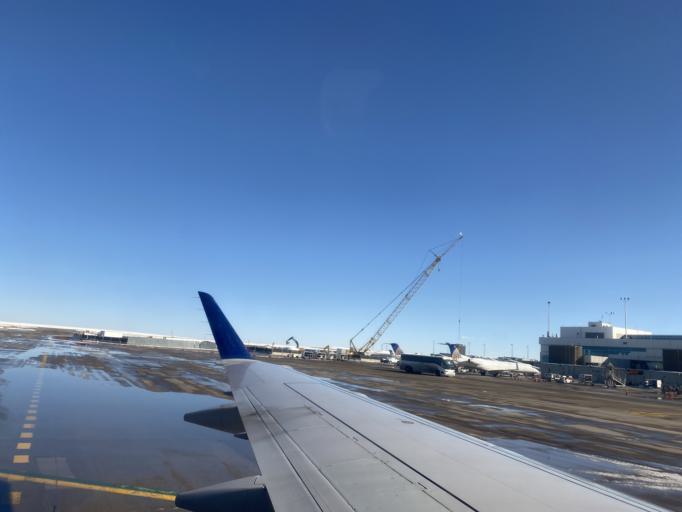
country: US
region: Colorado
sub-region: Weld County
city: Lochbuie
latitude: 39.8603
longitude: -104.6694
